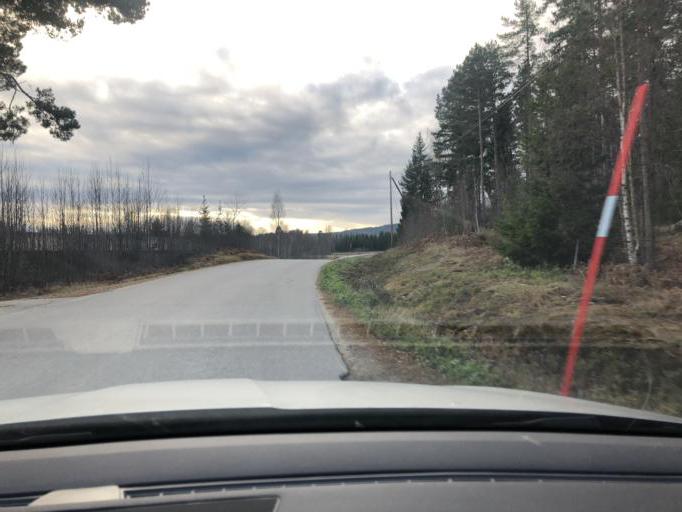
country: SE
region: Gaevleborg
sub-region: Hudiksvalls Kommun
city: Sorforsa
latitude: 61.7061
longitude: 16.9458
